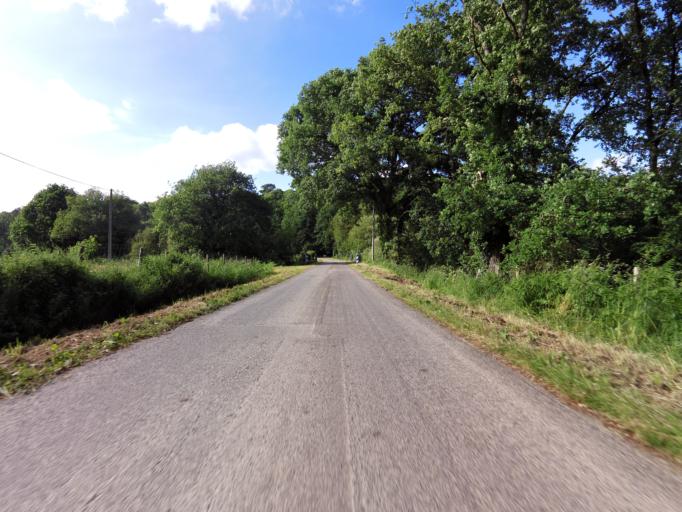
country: FR
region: Brittany
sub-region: Departement du Morbihan
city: Molac
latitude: 47.7180
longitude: -2.4140
